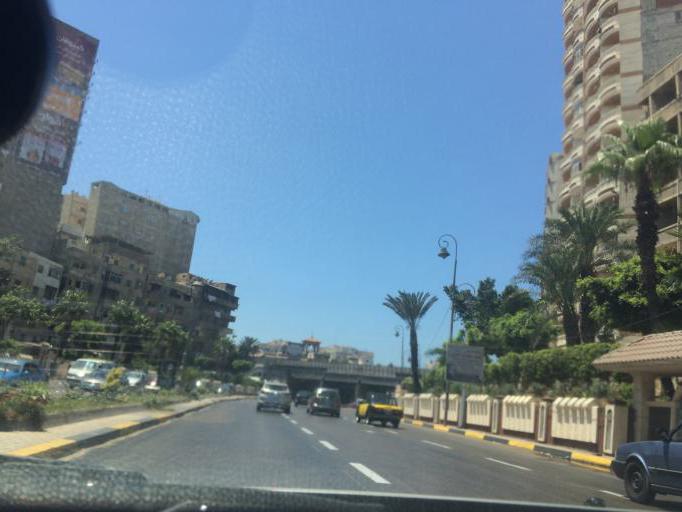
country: EG
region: Alexandria
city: Alexandria
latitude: 31.1962
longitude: 29.9189
